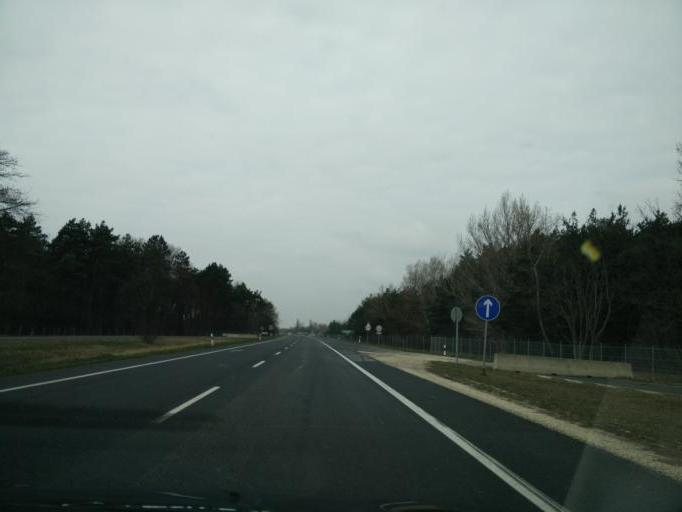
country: HU
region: Gyor-Moson-Sopron
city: Toltestava
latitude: 47.7112
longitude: 17.7441
